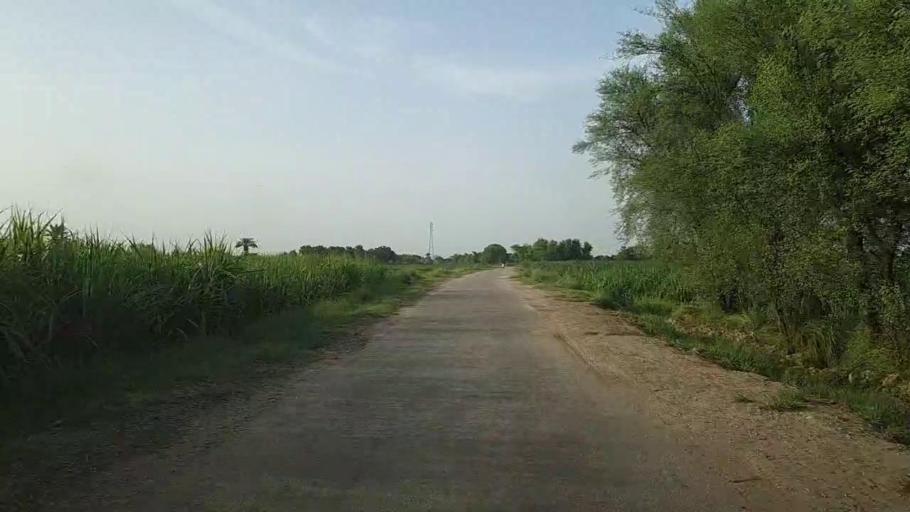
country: PK
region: Sindh
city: Bhiria
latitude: 26.9039
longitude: 68.2632
